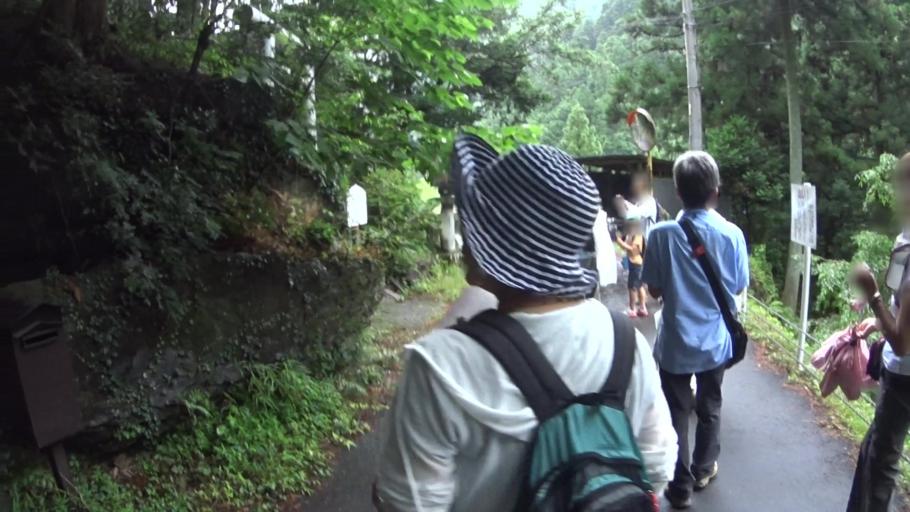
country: JP
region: Tokyo
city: Itsukaichi
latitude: 35.7942
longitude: 139.0691
